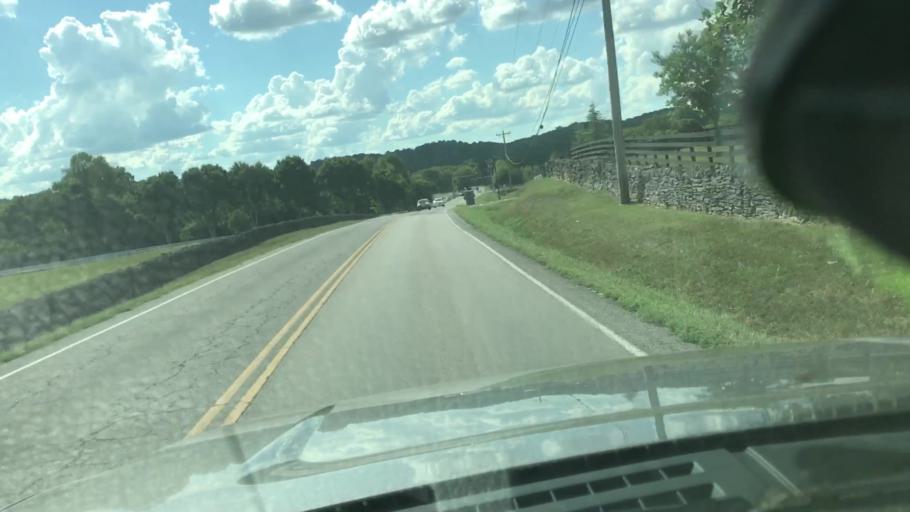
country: US
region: Tennessee
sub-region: Davidson County
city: Forest Hills
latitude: 36.0286
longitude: -86.9134
